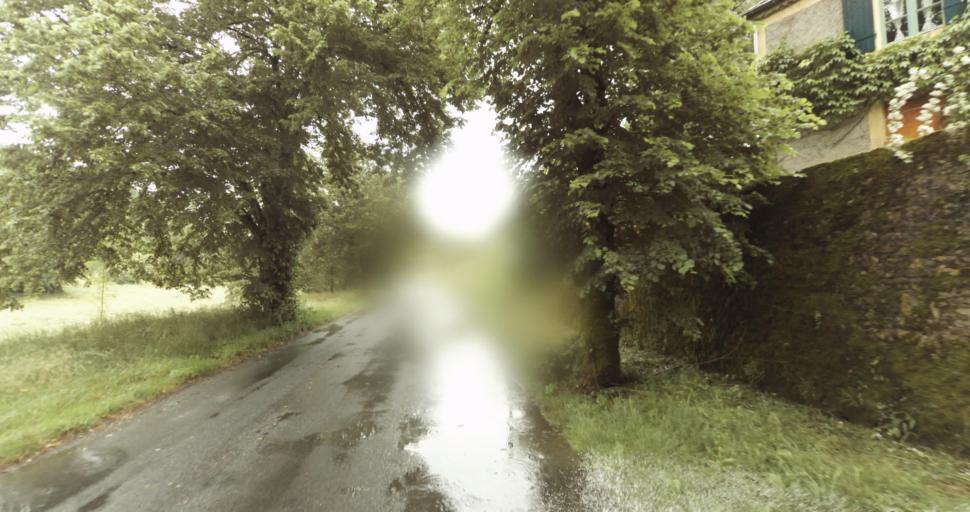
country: FR
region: Aquitaine
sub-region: Departement de la Dordogne
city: Beaumont-du-Perigord
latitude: 44.8121
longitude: 0.8673
